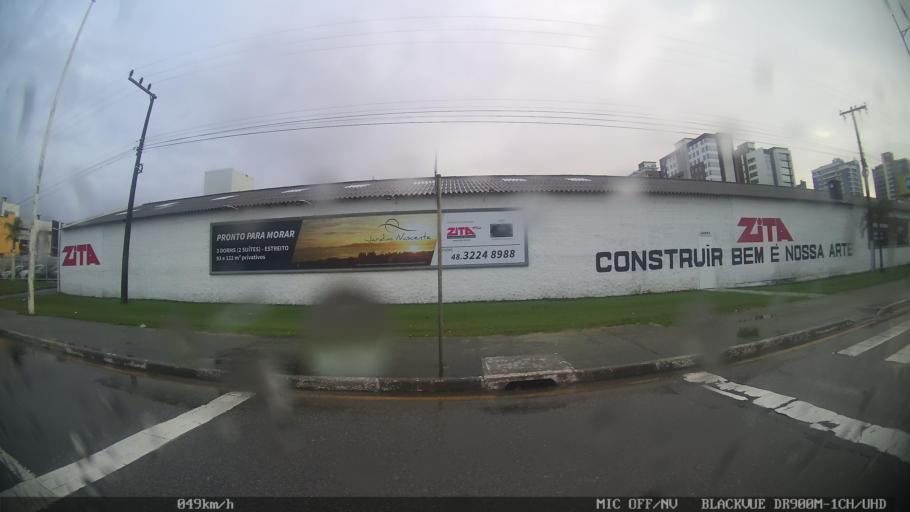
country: BR
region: Santa Catarina
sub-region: Sao Jose
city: Campinas
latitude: -27.6018
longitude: -48.6116
